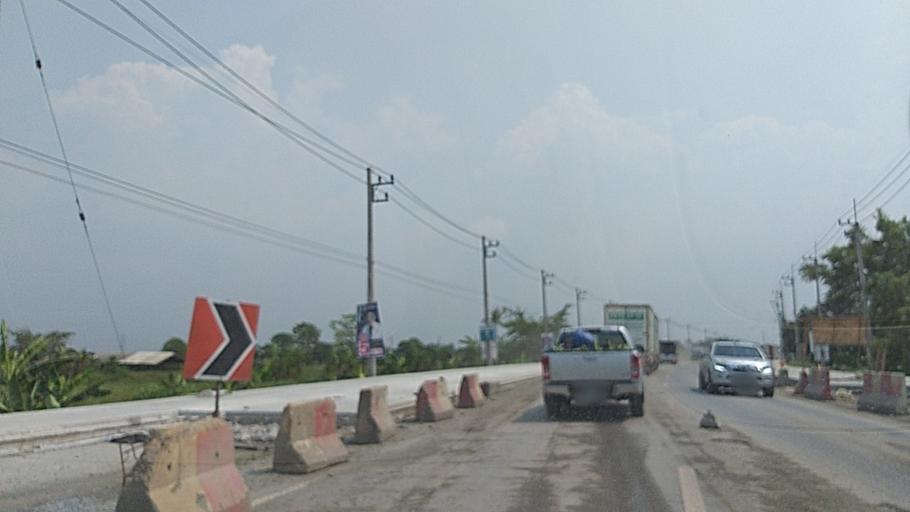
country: TH
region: Chon Buri
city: Phanat Nikhom
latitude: 13.4075
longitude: 101.1899
